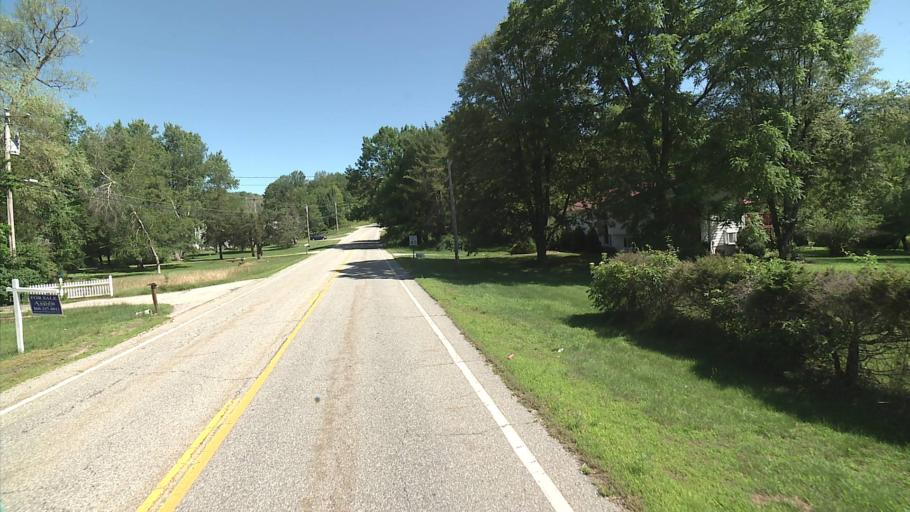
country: US
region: Connecticut
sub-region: Windham County
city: Willimantic
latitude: 41.6562
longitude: -72.2273
